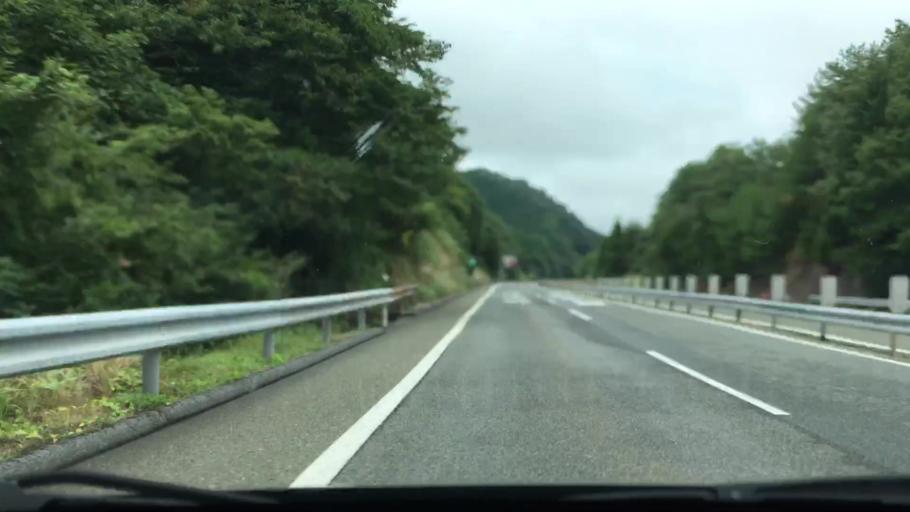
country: JP
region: Hiroshima
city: Shobara
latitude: 34.8717
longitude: 133.1181
